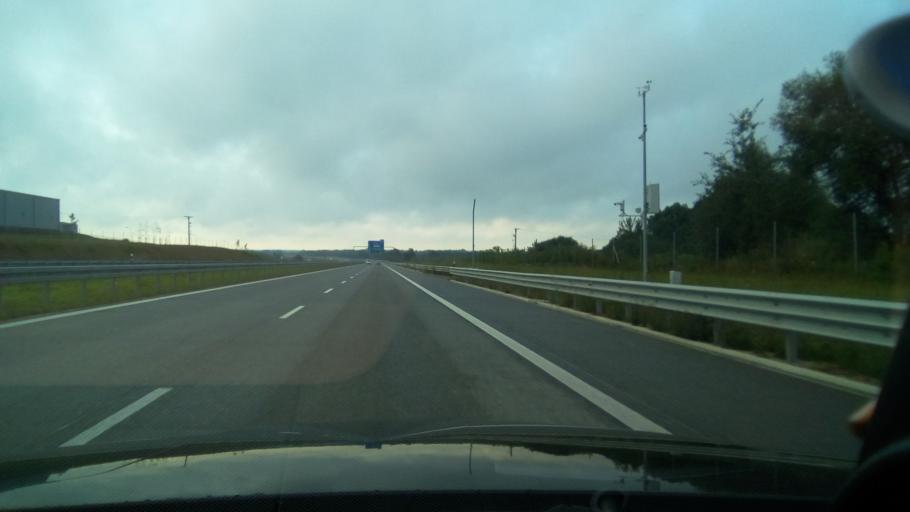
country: PL
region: Silesian Voivodeship
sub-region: Powiat czestochowski
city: Konopiska
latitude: 50.7600
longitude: 19.0227
